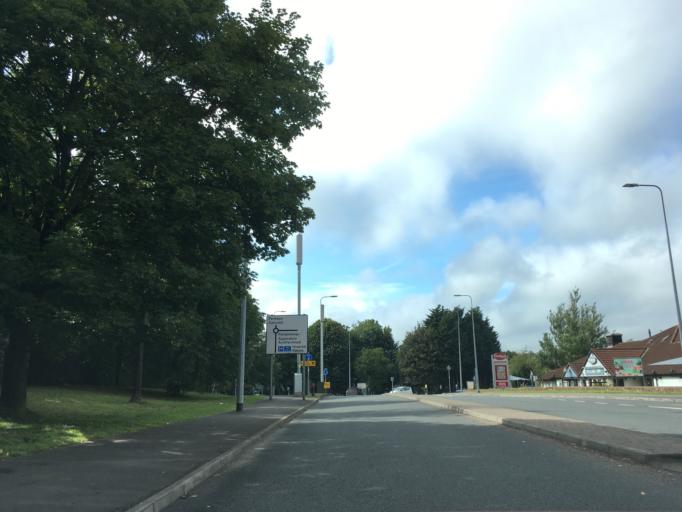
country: GB
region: Wales
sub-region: Cardiff
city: Cardiff
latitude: 51.5300
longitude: -3.1389
